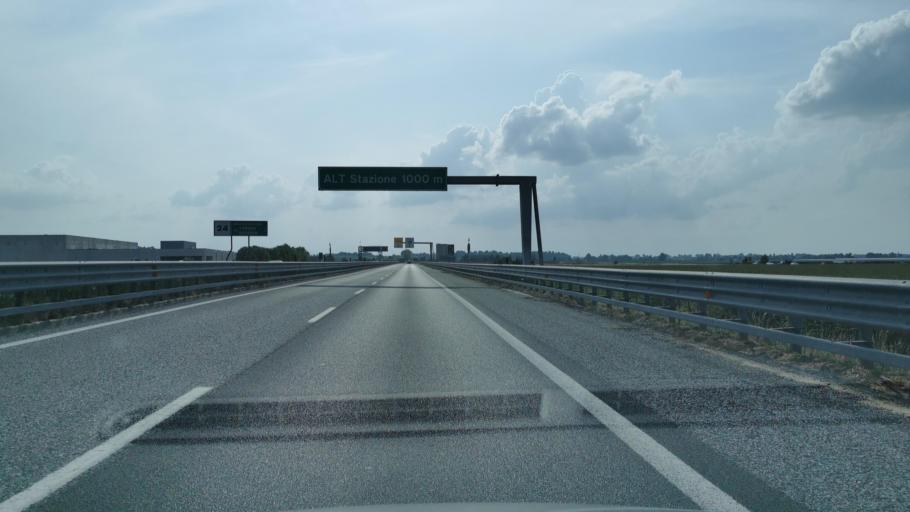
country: IT
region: Piedmont
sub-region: Provincia di Cuneo
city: Cervere
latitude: 44.6645
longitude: 7.7924
